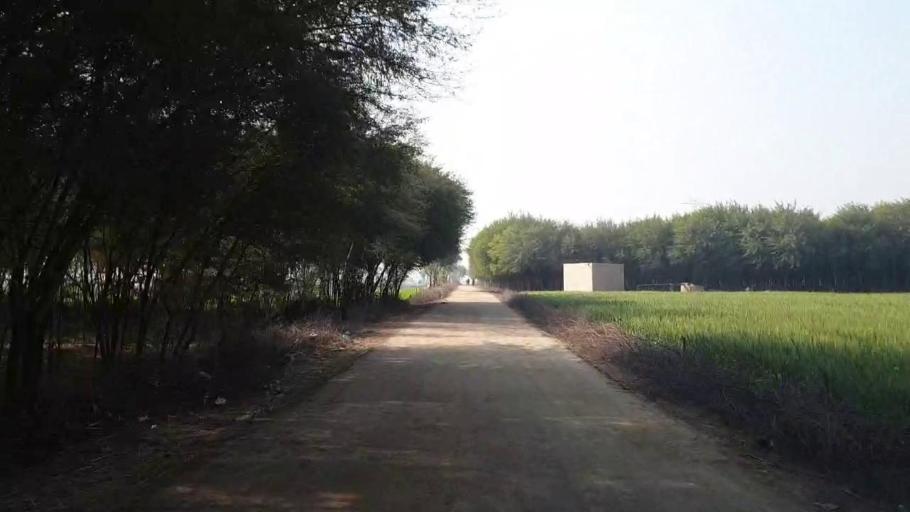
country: PK
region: Sindh
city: Matiari
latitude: 25.6742
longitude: 68.4944
